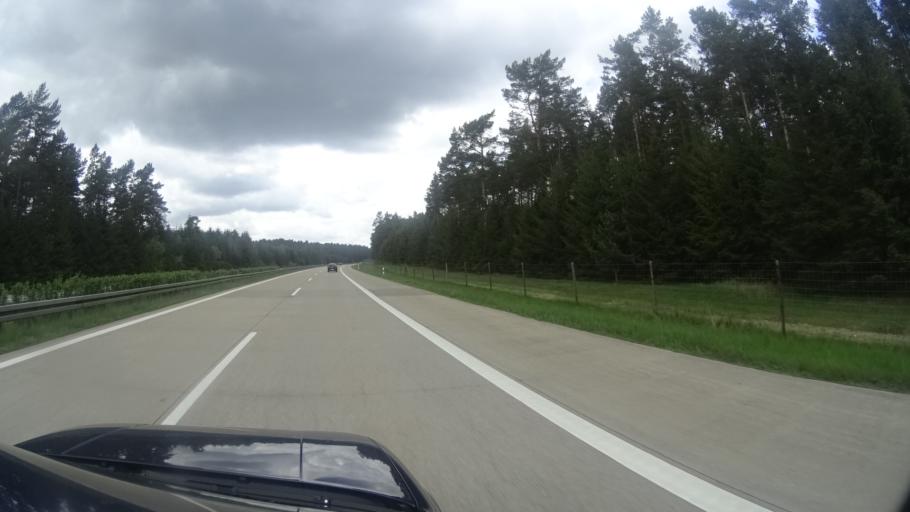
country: DE
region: Mecklenburg-Vorpommern
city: Krakow am See
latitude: 53.5526
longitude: 12.3224
